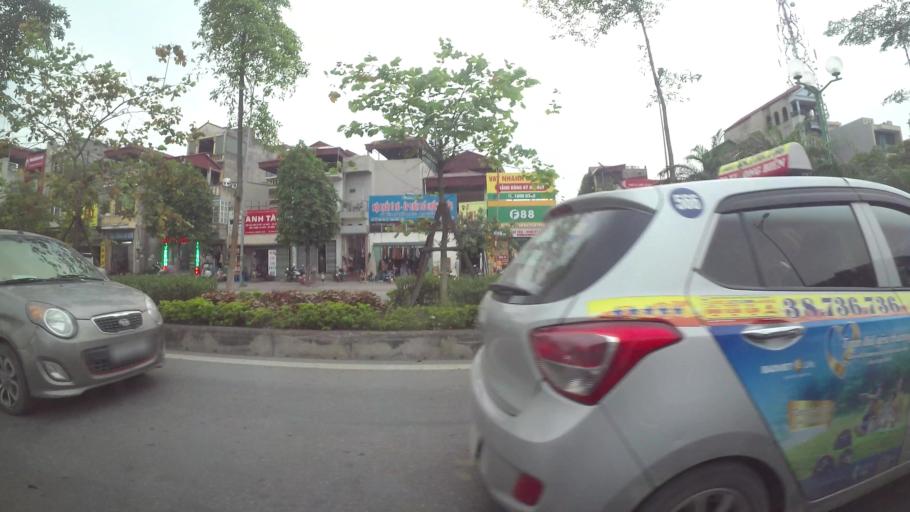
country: VN
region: Ha Noi
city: Hoan Kiem
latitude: 21.0572
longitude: 105.8901
